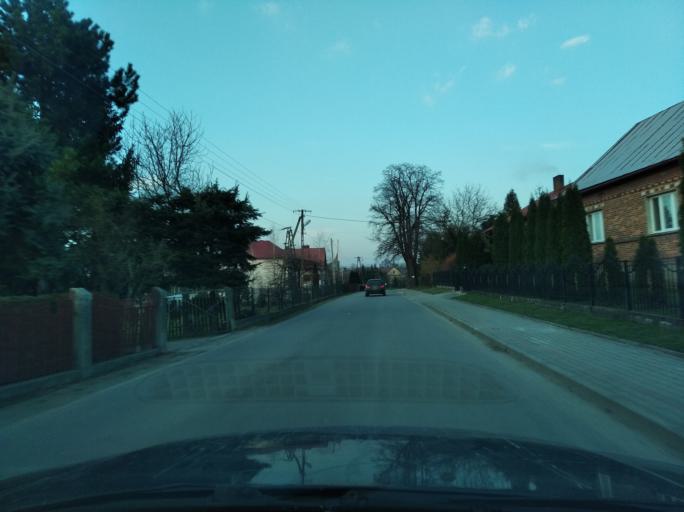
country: PL
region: Subcarpathian Voivodeship
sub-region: Powiat przeworski
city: Zurawiczki
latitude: 50.0257
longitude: 22.5088
